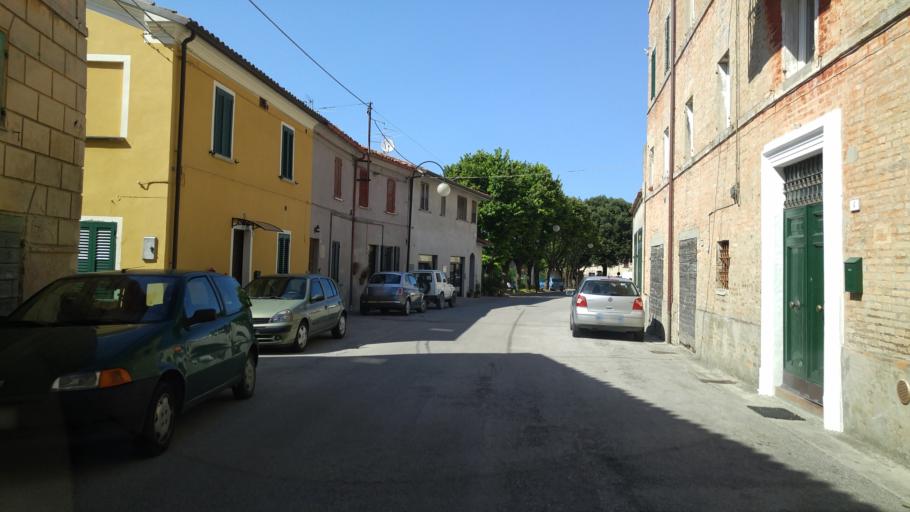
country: IT
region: The Marches
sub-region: Provincia di Pesaro e Urbino
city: Sant'Angelo in Lizzola
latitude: 43.8272
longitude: 12.8020
